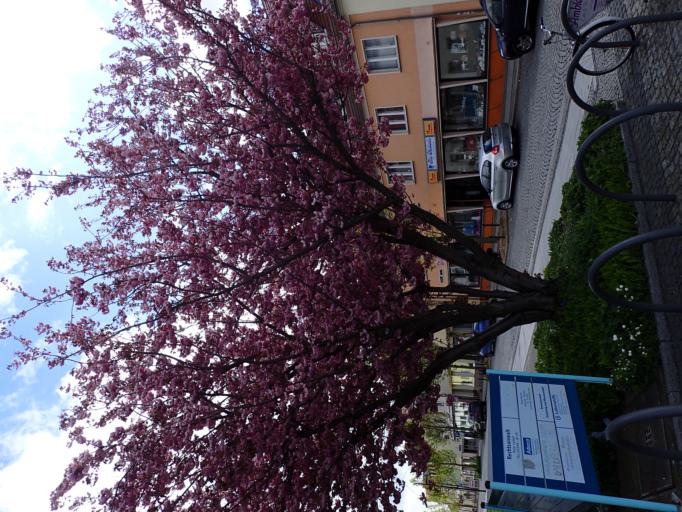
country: DE
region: Brandenburg
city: Luebben
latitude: 51.9414
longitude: 13.8970
